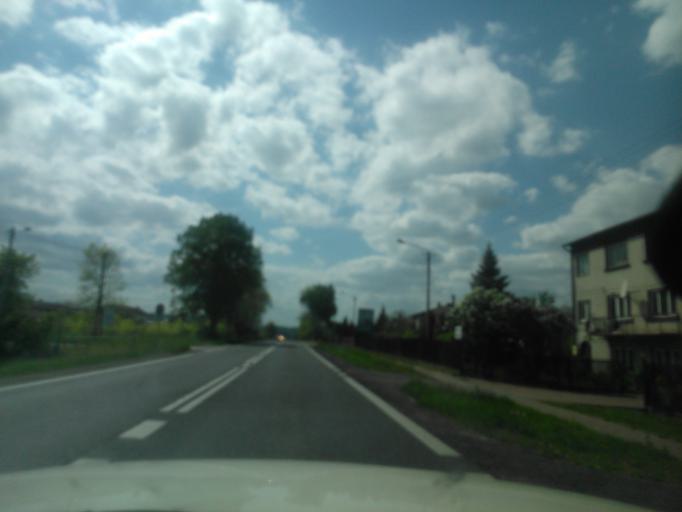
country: PL
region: Swietokrzyskie
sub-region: Powiat ostrowiecki
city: Kunow
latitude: 50.9493
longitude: 21.3135
